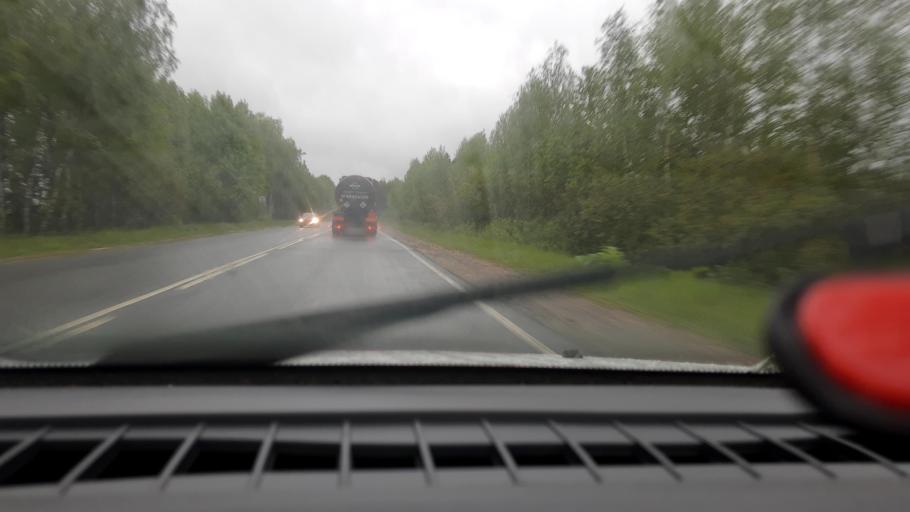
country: RU
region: Nizjnij Novgorod
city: Vladimirskoye
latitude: 56.8838
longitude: 44.9781
